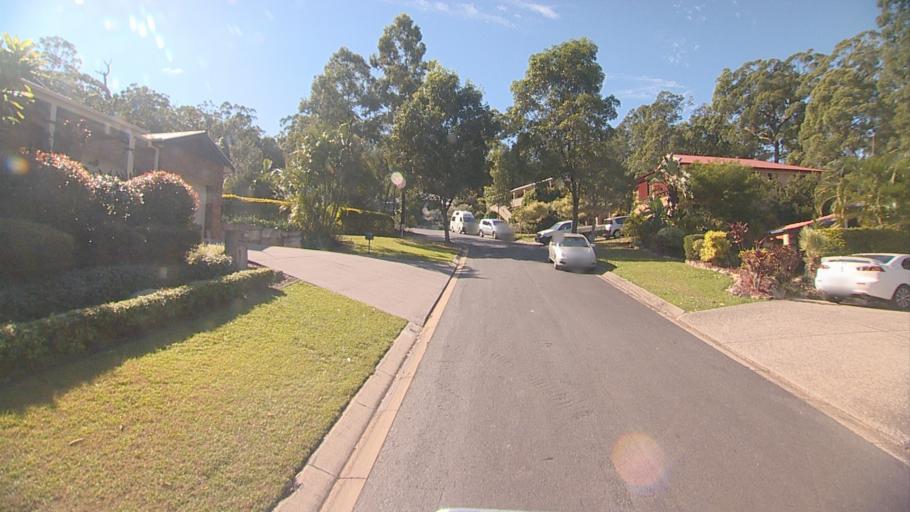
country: AU
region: Queensland
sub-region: Logan
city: Slacks Creek
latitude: -27.6362
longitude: 153.1789
